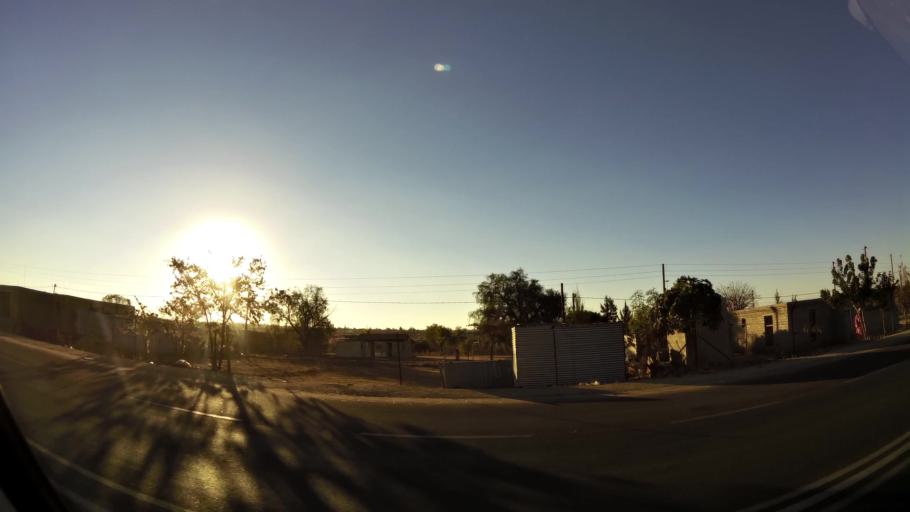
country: ZA
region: Limpopo
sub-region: Capricorn District Municipality
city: Polokwane
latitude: -23.8334
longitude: 29.3678
